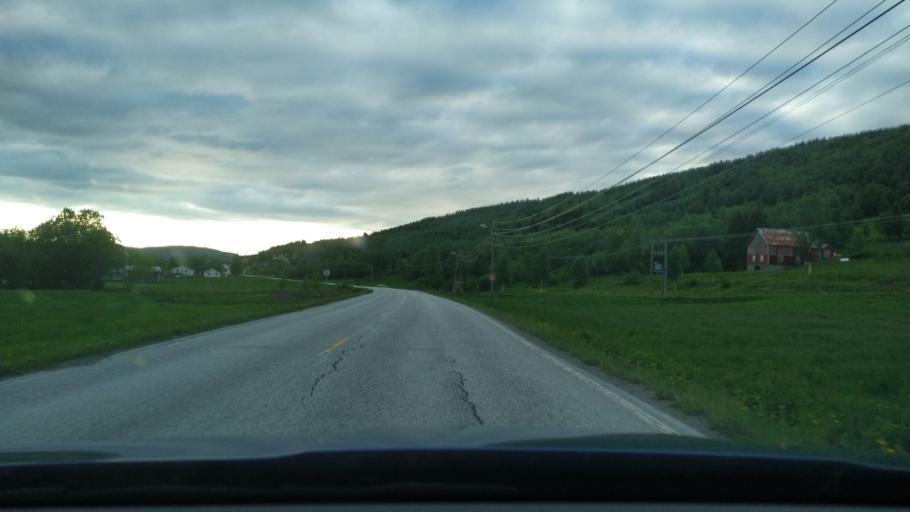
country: NO
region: Troms
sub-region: Sorreisa
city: Sorreisa
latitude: 69.1255
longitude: 18.2148
